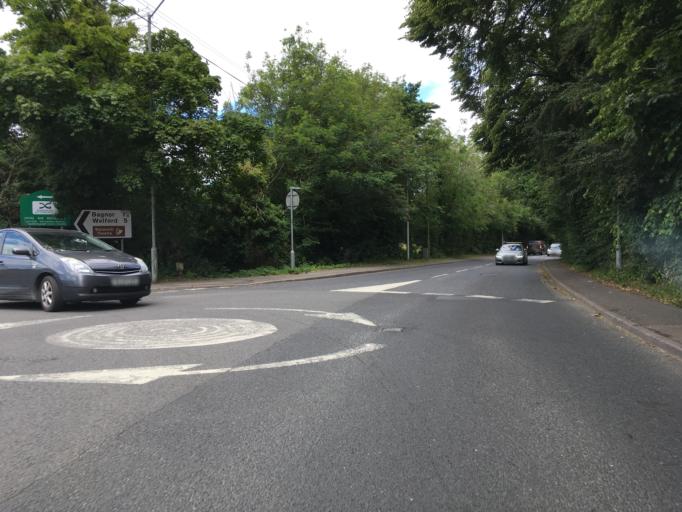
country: GB
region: England
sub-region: West Berkshire
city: Newbury
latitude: 51.4127
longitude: -1.3322
